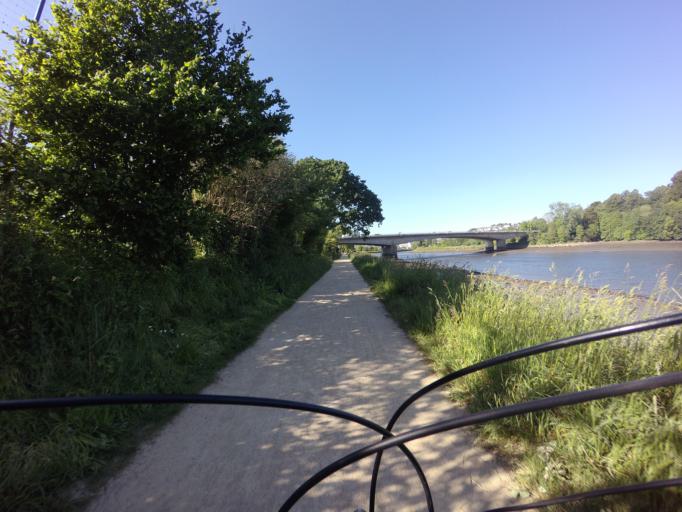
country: FR
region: Brittany
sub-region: Departement du Finistere
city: Quimper
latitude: 47.9826
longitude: -4.1177
